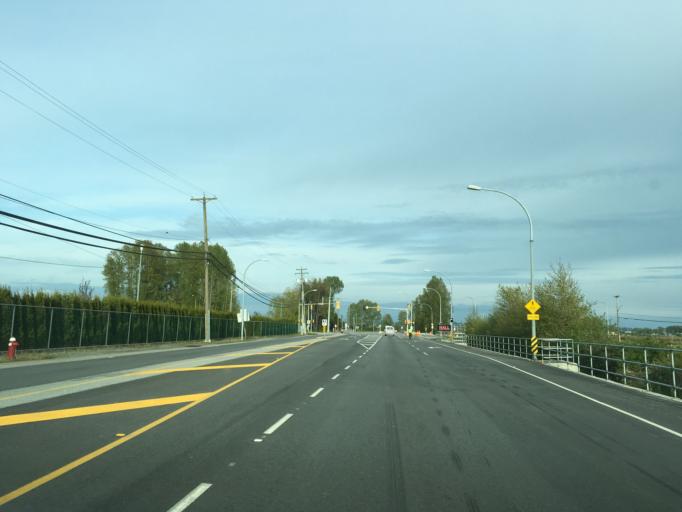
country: CA
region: British Columbia
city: Ladner
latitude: 49.1698
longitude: -123.0151
